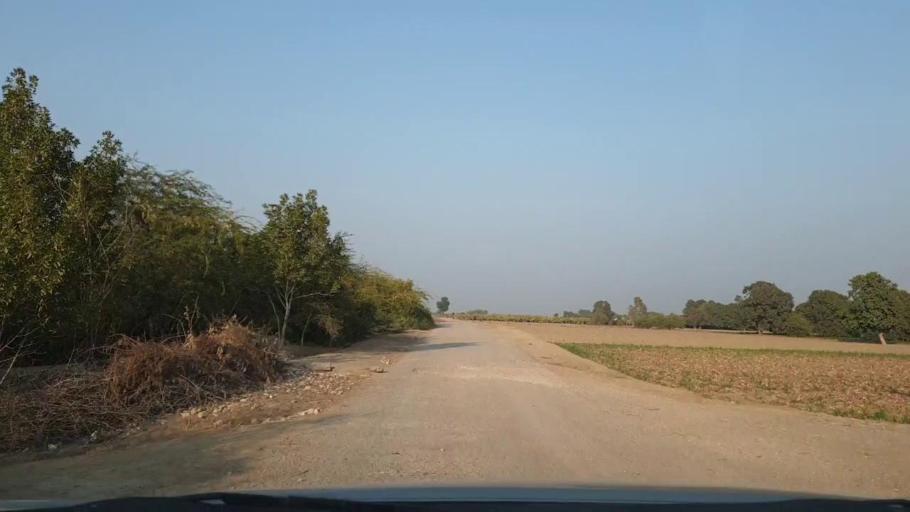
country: PK
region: Sindh
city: Tando Adam
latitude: 25.6977
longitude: 68.6373
